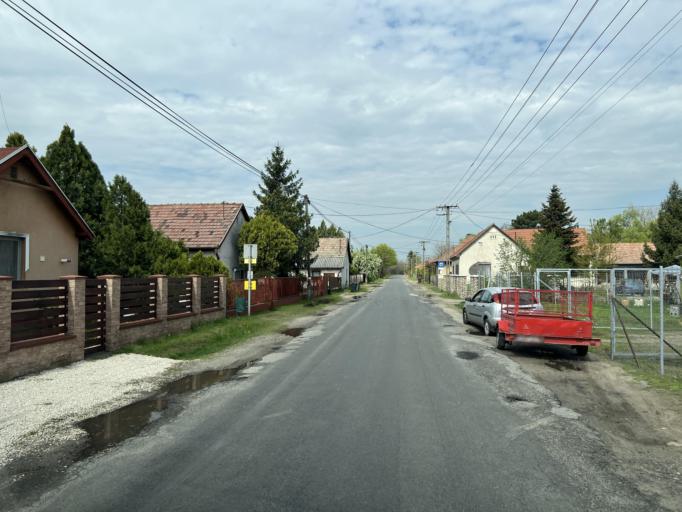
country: HU
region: Pest
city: Taborfalva
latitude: 47.1252
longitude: 19.4800
